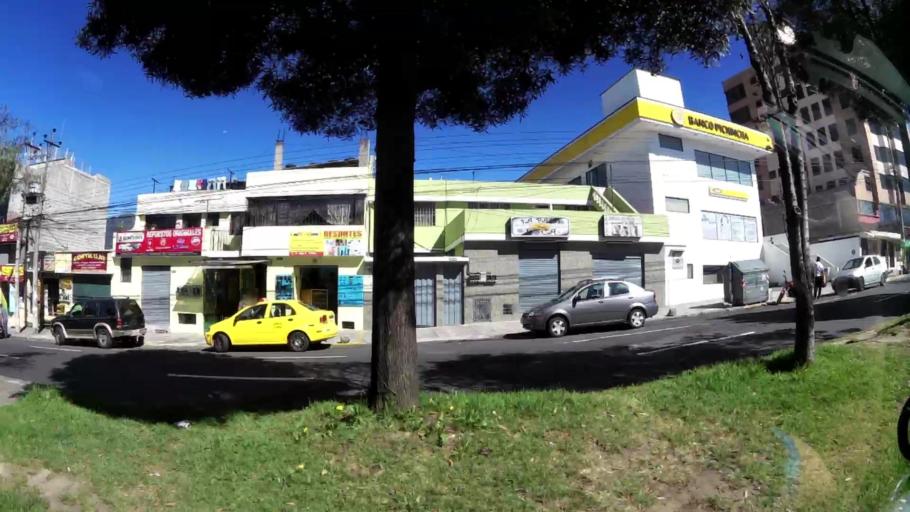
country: EC
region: Pichincha
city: Quito
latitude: -0.1404
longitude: -78.4734
